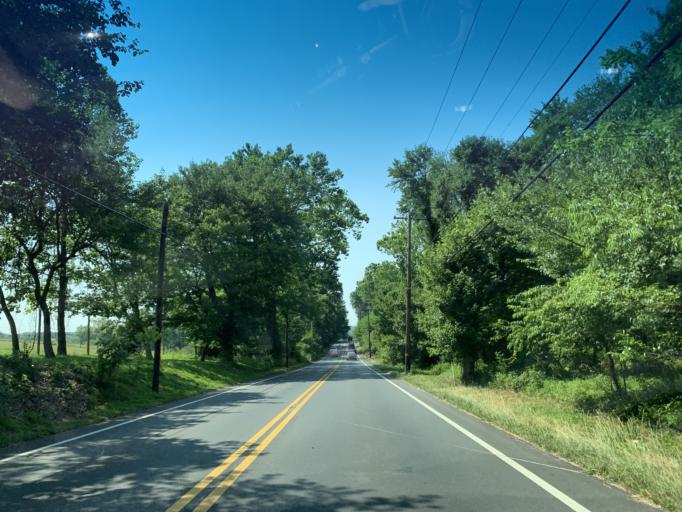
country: US
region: Maryland
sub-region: Montgomery County
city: Darnestown
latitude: 39.1238
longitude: -77.3255
